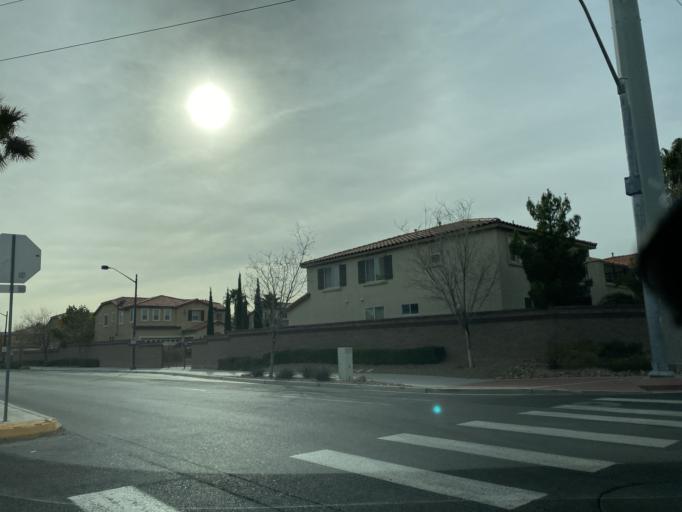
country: US
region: Nevada
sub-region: Clark County
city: Summerlin South
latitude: 36.2991
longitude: -115.2968
